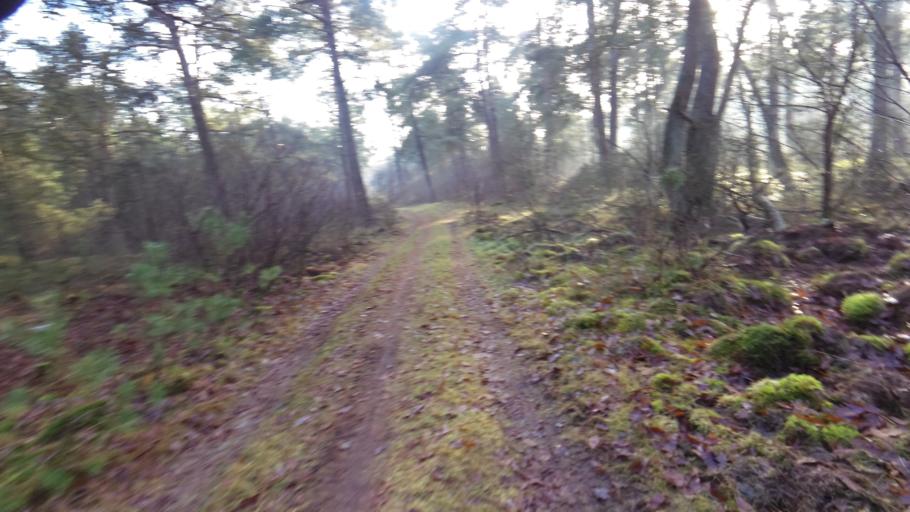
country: NL
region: Gelderland
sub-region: Gemeente Barneveld
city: Garderen
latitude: 52.2043
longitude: 5.7375
